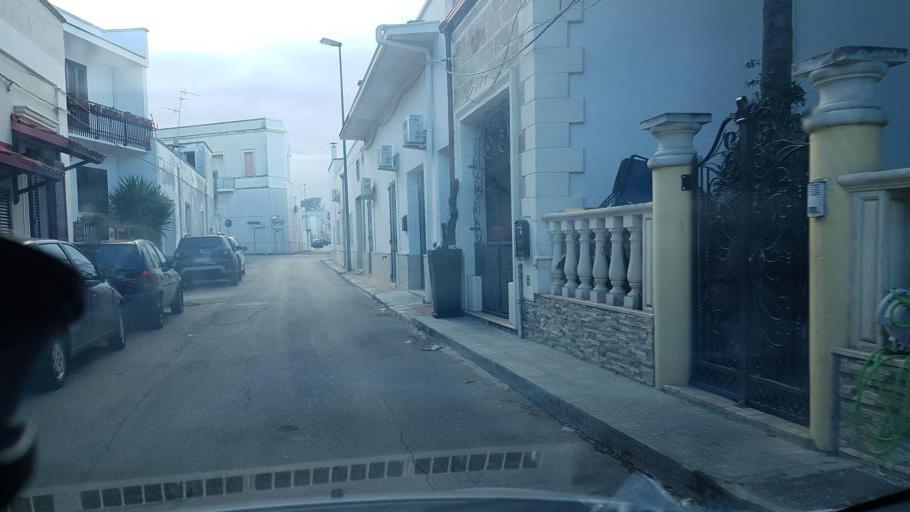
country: IT
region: Apulia
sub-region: Provincia di Lecce
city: Veglie
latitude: 40.3383
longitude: 17.9704
